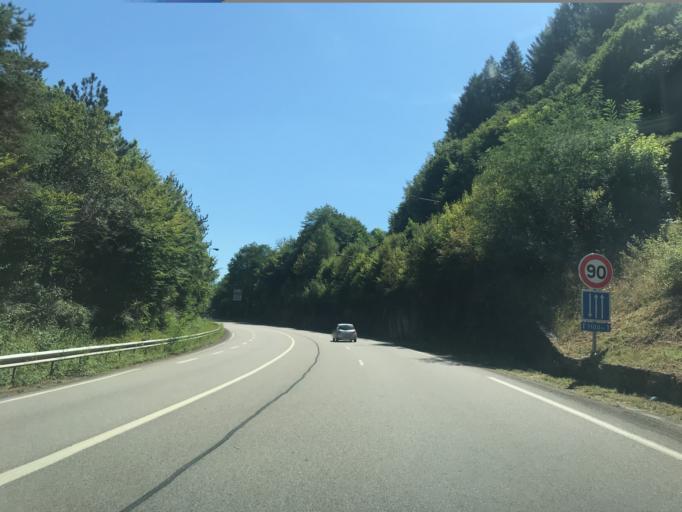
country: FR
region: Limousin
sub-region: Departement de la Correze
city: Laguenne
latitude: 45.2489
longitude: 1.7664
